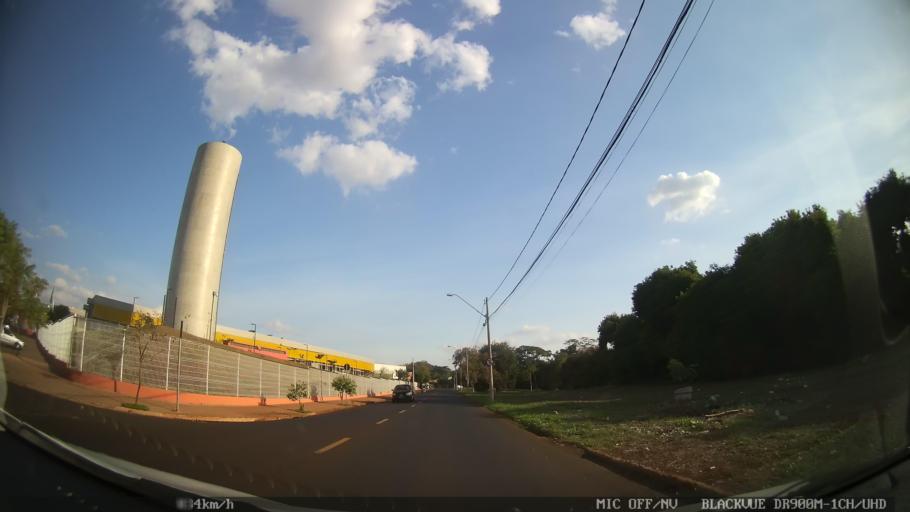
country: BR
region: Sao Paulo
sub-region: Ribeirao Preto
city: Ribeirao Preto
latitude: -21.1463
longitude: -47.8357
